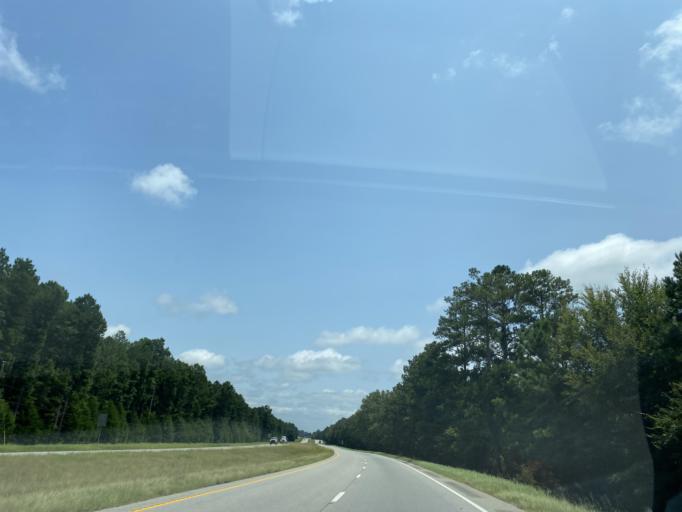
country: US
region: Georgia
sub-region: Telfair County
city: Lumber City
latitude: 31.9073
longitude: -82.6644
